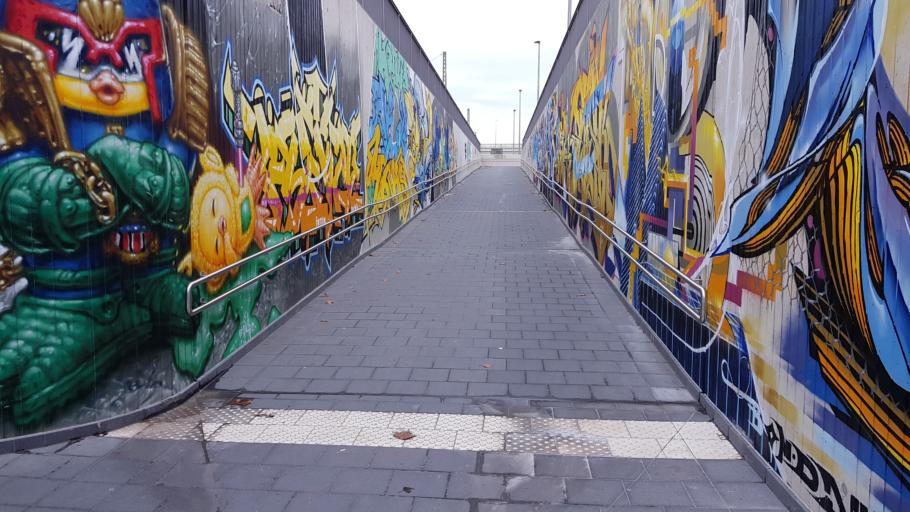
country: DE
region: Bavaria
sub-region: Regierungsbezirk Mittelfranken
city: Baiersdorf
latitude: 49.6560
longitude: 11.0372
